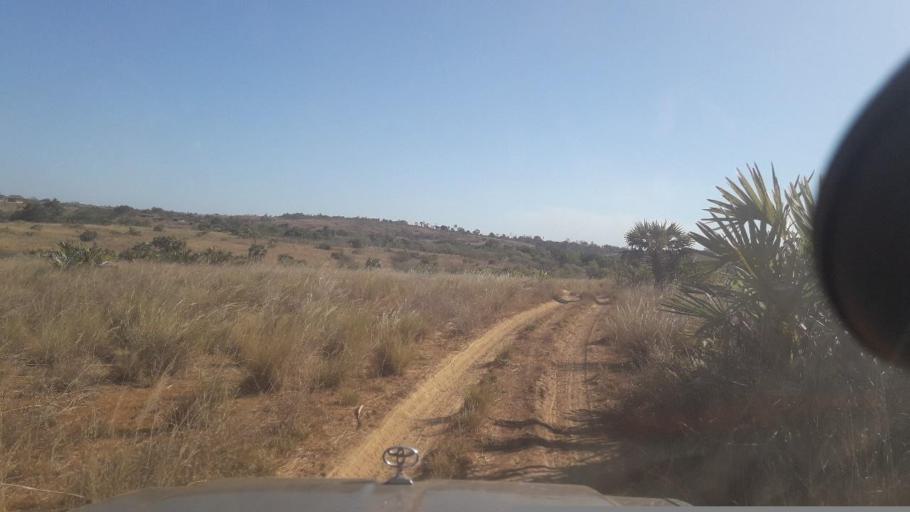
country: MG
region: Boeny
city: Sitampiky
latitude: -16.3753
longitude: 45.5917
